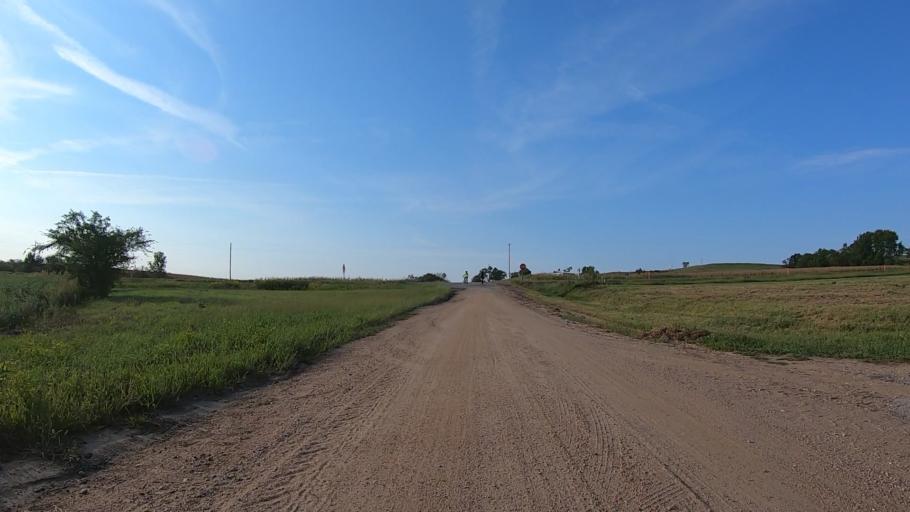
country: US
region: Kansas
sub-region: Marshall County
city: Blue Rapids
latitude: 39.6904
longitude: -96.7792
